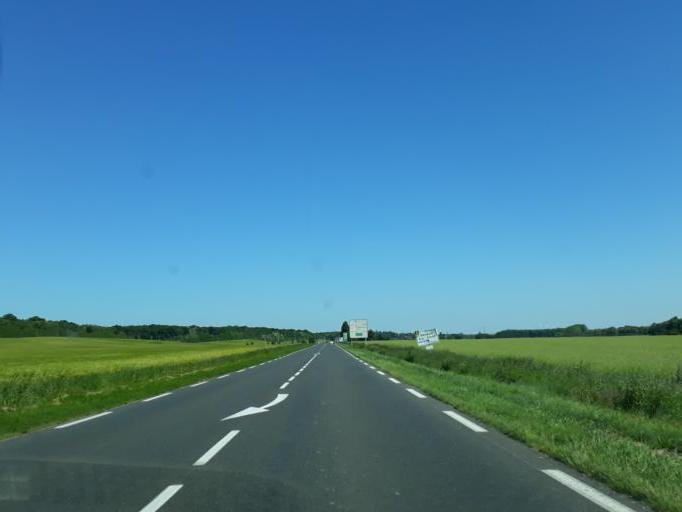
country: FR
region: Centre
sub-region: Departement du Loiret
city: Saint-Brisson-sur-Loire
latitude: 47.6632
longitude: 2.7052
